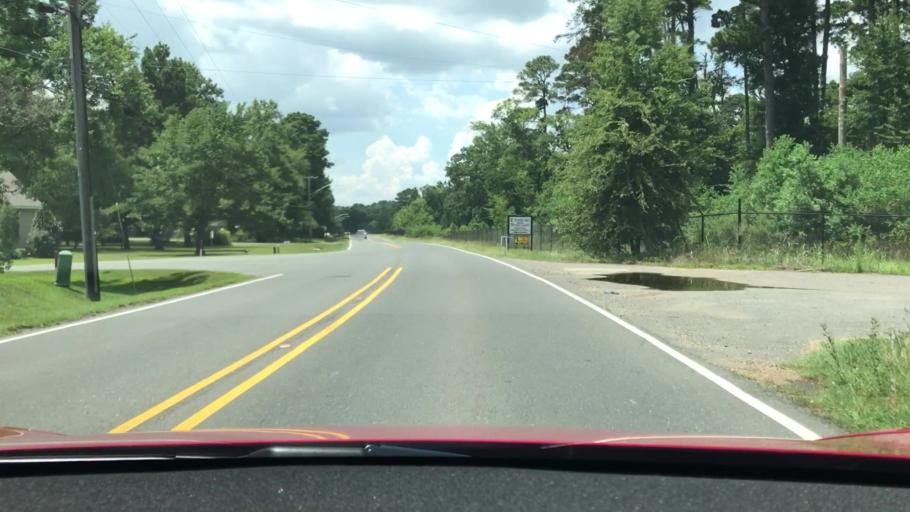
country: US
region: Louisiana
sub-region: Bossier Parish
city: Bossier City
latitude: 32.3866
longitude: -93.7177
